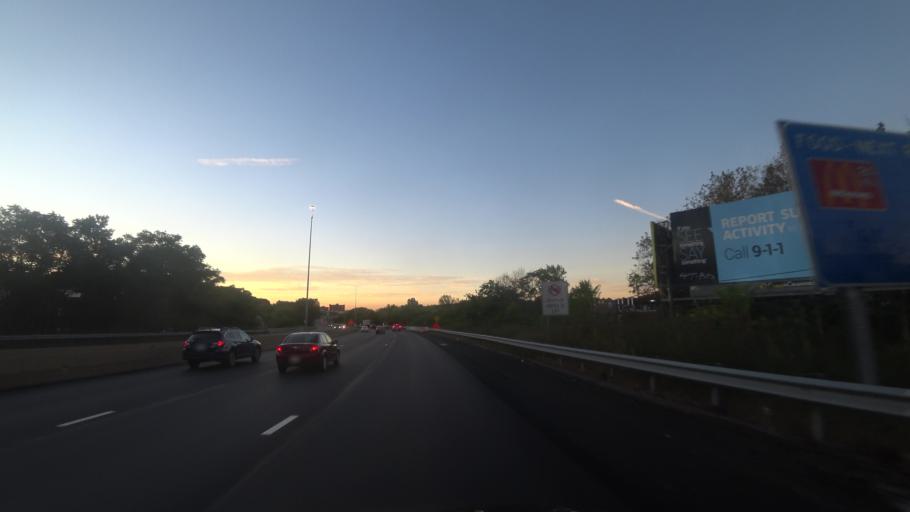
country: US
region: Massachusetts
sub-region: Suffolk County
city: Revere
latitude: 42.4133
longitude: -71.0311
